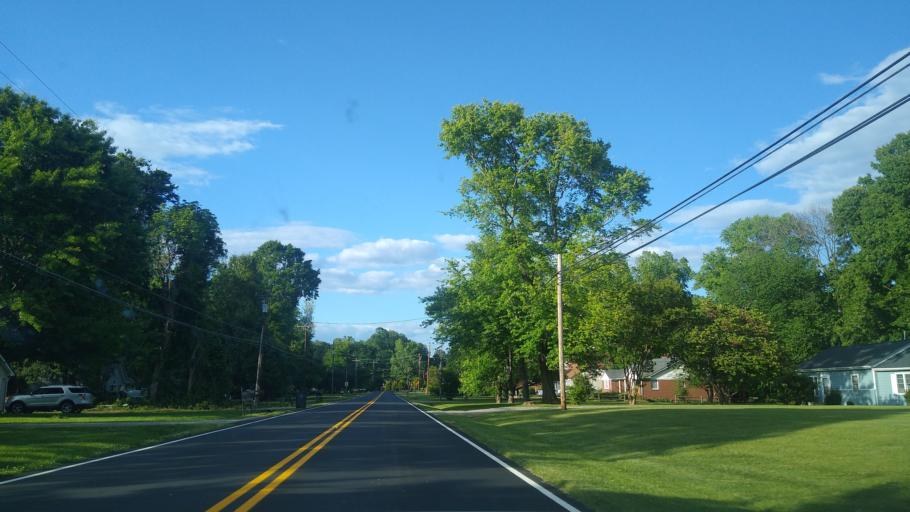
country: US
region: North Carolina
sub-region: Guilford County
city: McLeansville
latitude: 36.1658
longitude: -79.7296
